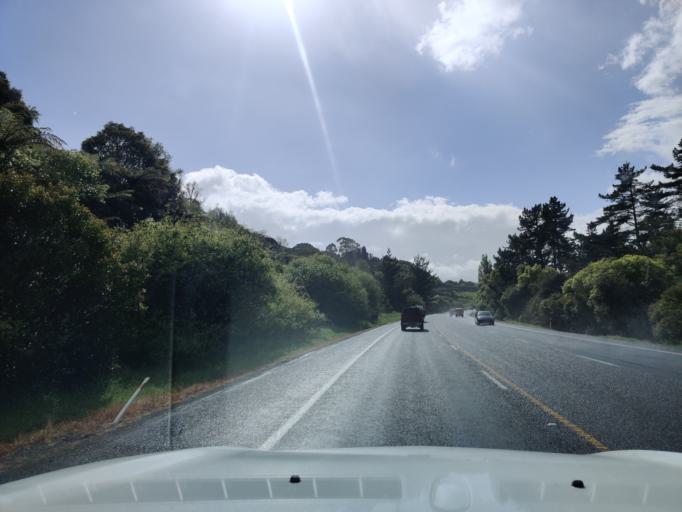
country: NZ
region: Waikato
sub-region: Matamata-Piako District
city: Matamata
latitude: -37.9466
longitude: 175.6460
